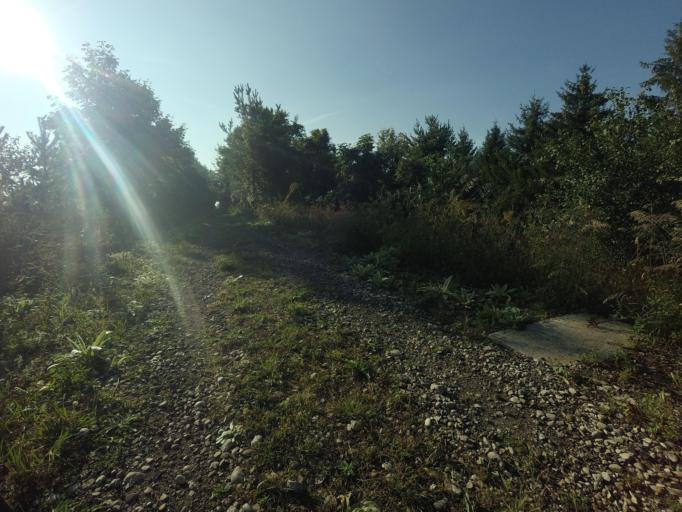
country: CA
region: Ontario
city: Goderich
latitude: 43.7583
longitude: -81.5179
